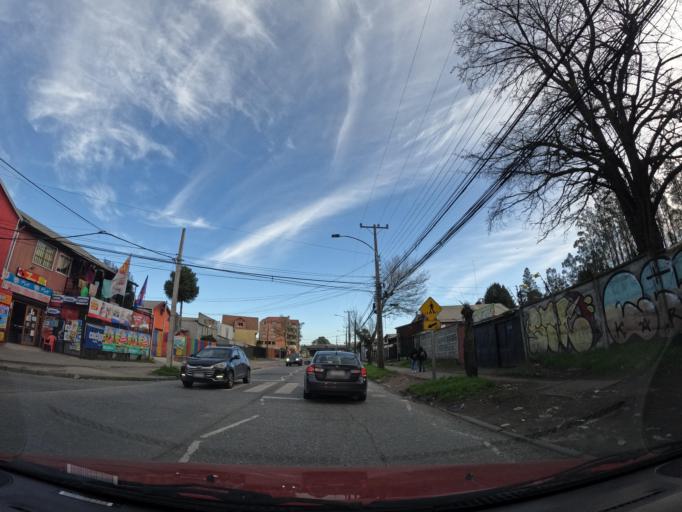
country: CL
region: Biobio
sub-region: Provincia de Concepcion
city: Concepcion
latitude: -36.8066
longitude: -73.0319
